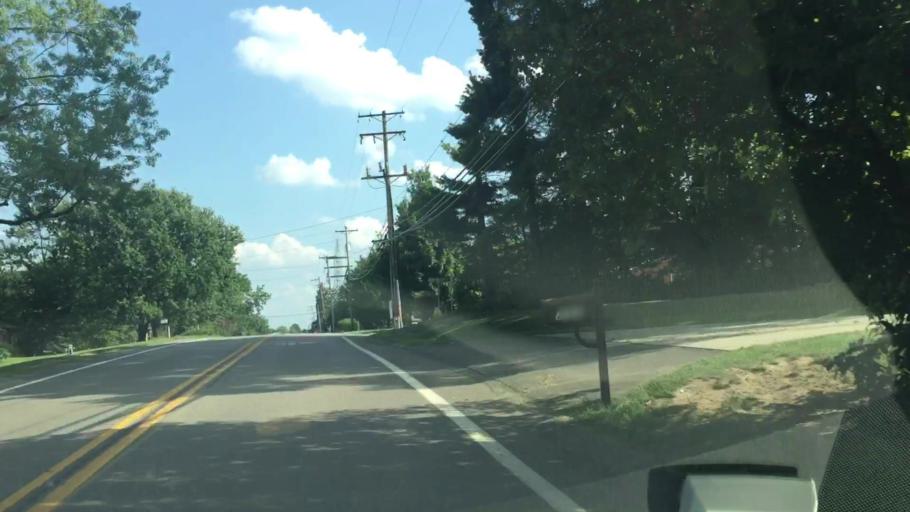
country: US
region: Pennsylvania
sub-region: Allegheny County
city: Franklin Park
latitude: 40.5708
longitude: -80.1056
